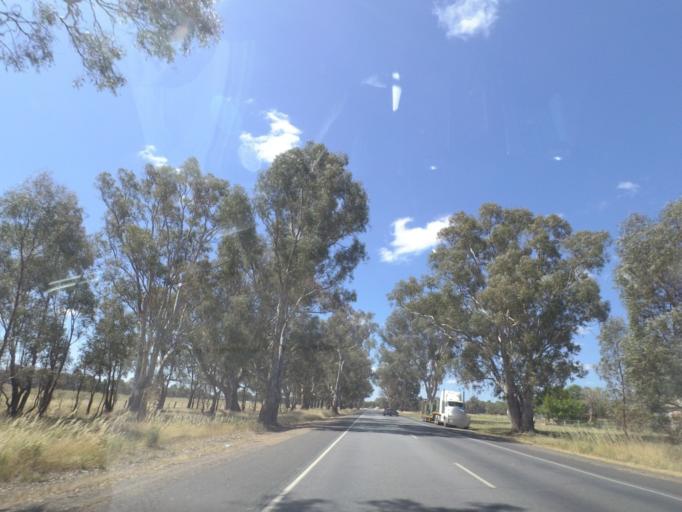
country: AU
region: Victoria
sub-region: Wangaratta
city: Wangaratta
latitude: -36.4021
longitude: 146.2758
